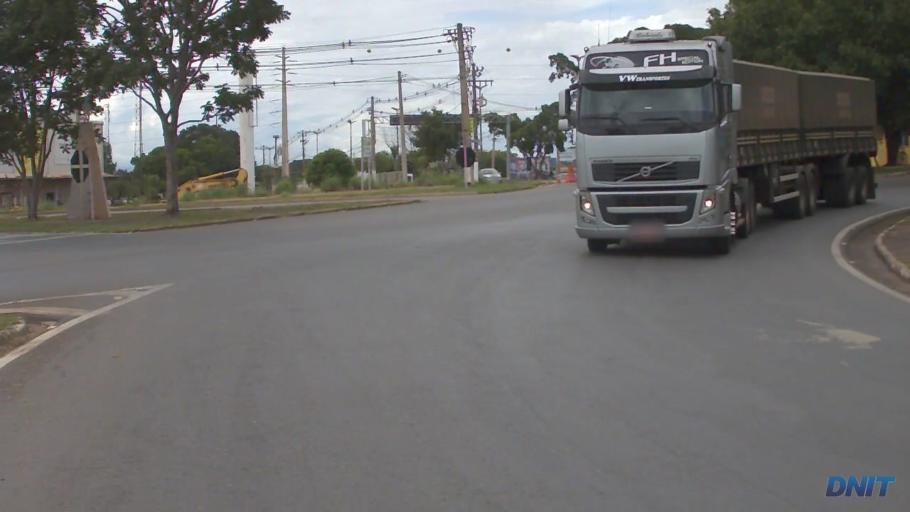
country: BR
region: Mato Grosso
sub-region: Varzea Grande
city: Varzea Grande
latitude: -15.6493
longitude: -56.1959
